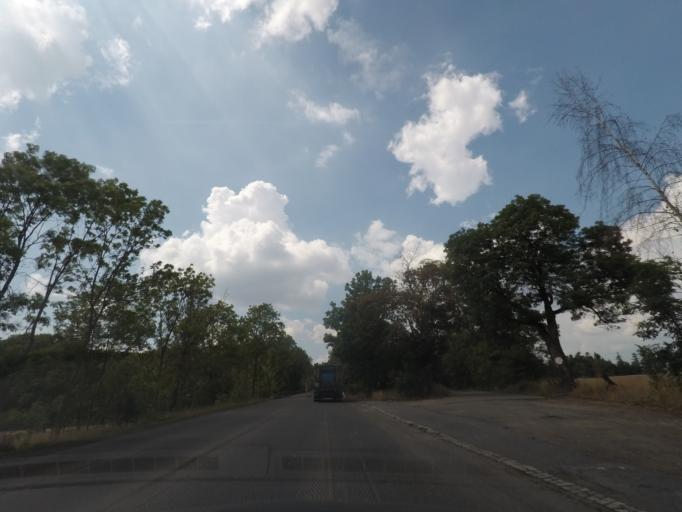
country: CZ
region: Olomoucky
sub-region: Okres Sumperk
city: Mohelnice
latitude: 49.7772
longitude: 16.8581
